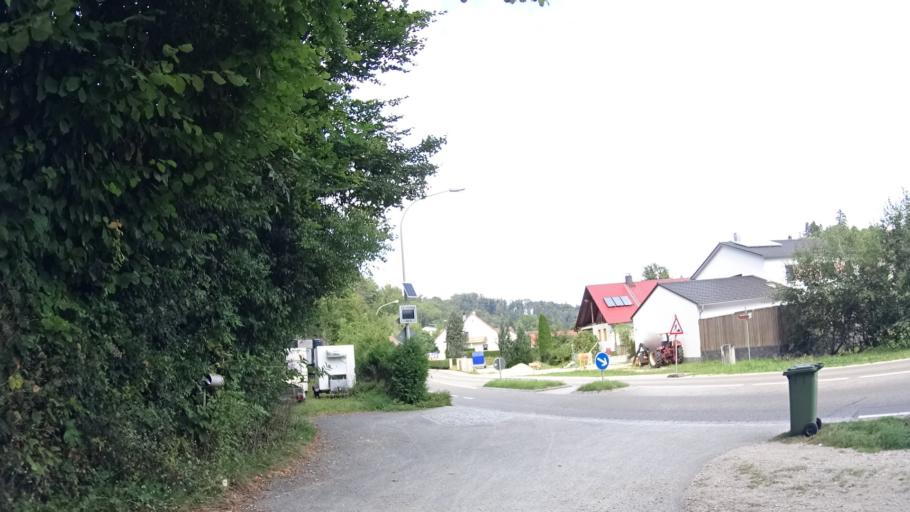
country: DE
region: Bavaria
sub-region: Lower Bavaria
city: Riedenburg
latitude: 48.9190
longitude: 11.6828
